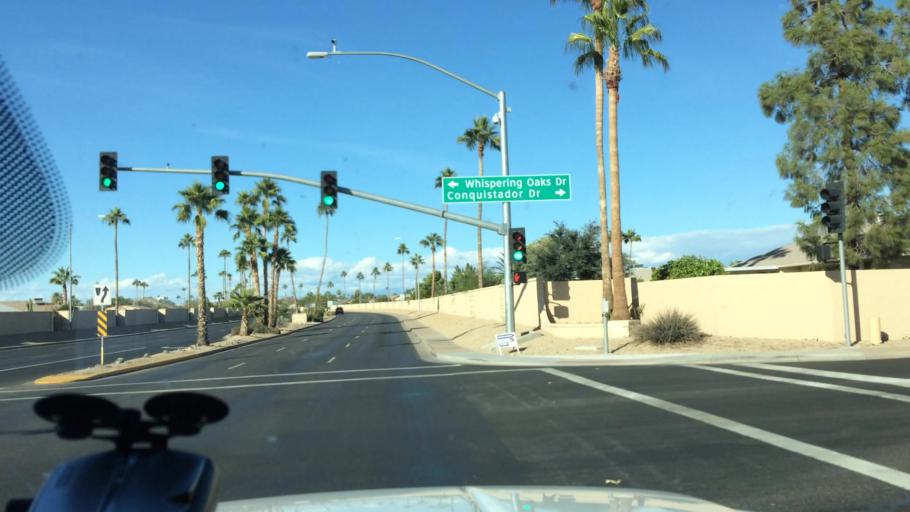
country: US
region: Arizona
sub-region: Maricopa County
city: Surprise
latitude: 33.6424
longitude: -112.3344
